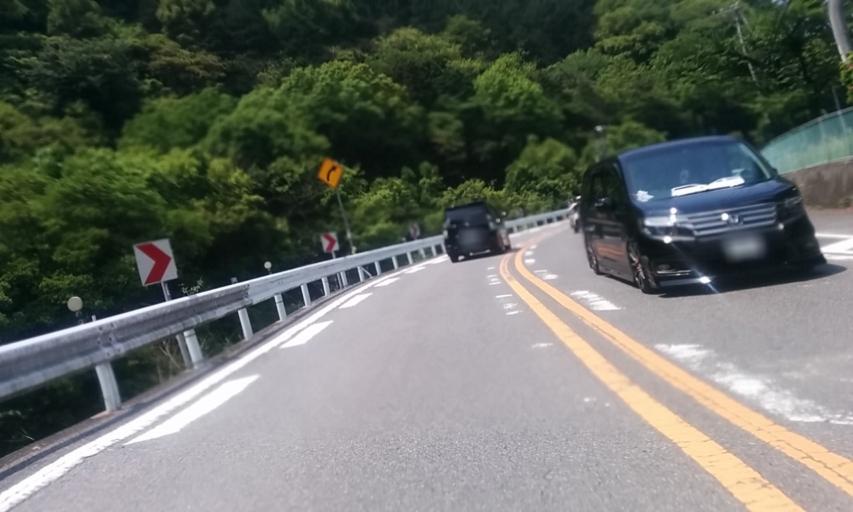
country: JP
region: Ehime
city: Niihama
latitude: 33.9189
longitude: 133.3091
